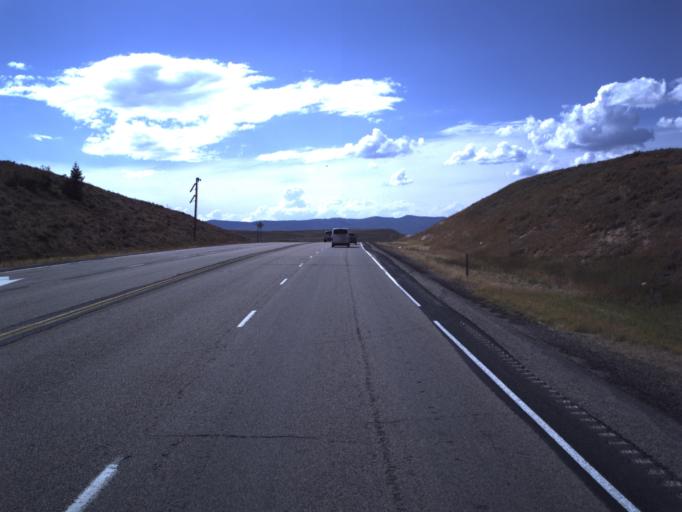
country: US
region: Utah
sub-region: Wasatch County
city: Heber
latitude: 40.1840
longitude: -111.0562
